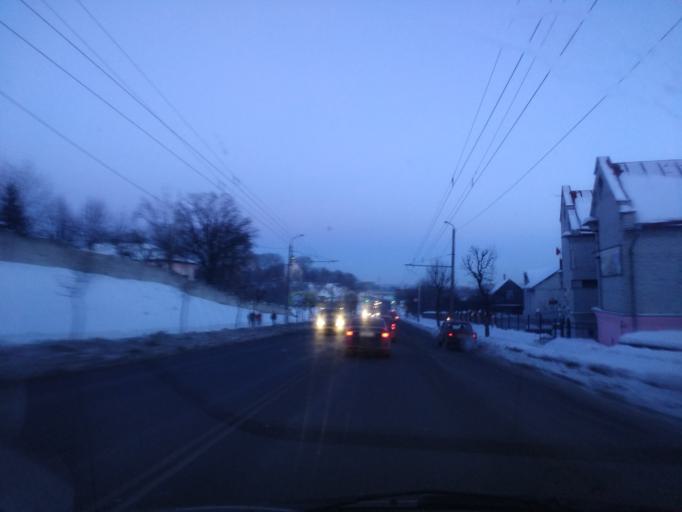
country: BY
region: Mogilev
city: Mahilyow
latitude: 53.8934
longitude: 30.3196
